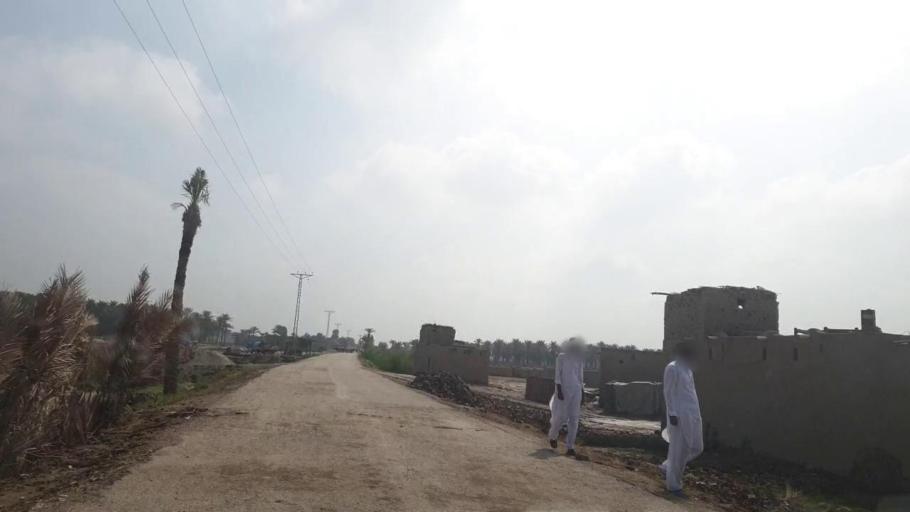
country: PK
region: Sindh
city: Khairpur
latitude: 27.5728
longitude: 68.7642
